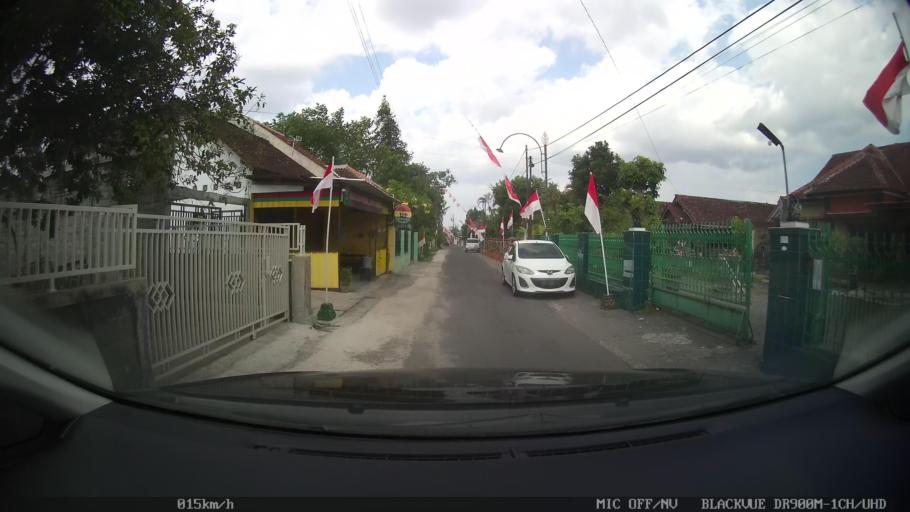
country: ID
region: Daerah Istimewa Yogyakarta
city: Gamping Lor
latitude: -7.8022
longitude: 110.3270
